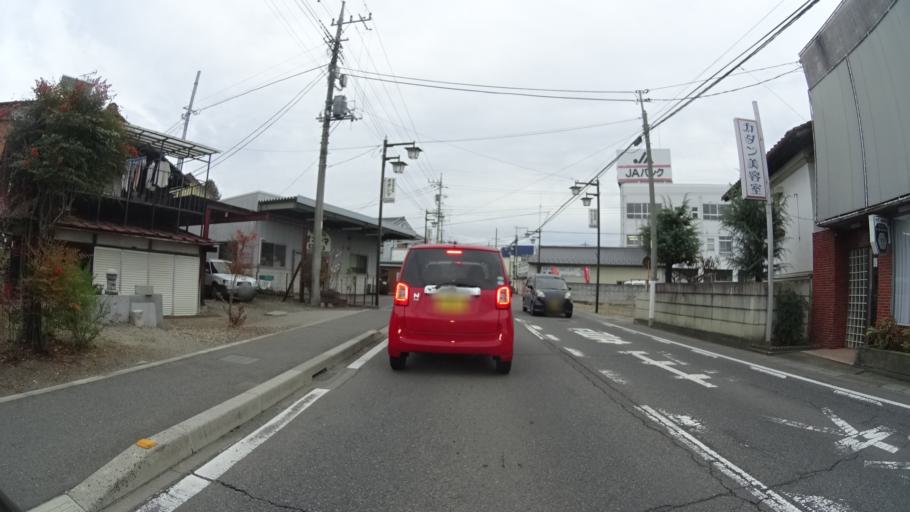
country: JP
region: Gunma
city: Numata
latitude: 36.6493
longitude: 139.0572
